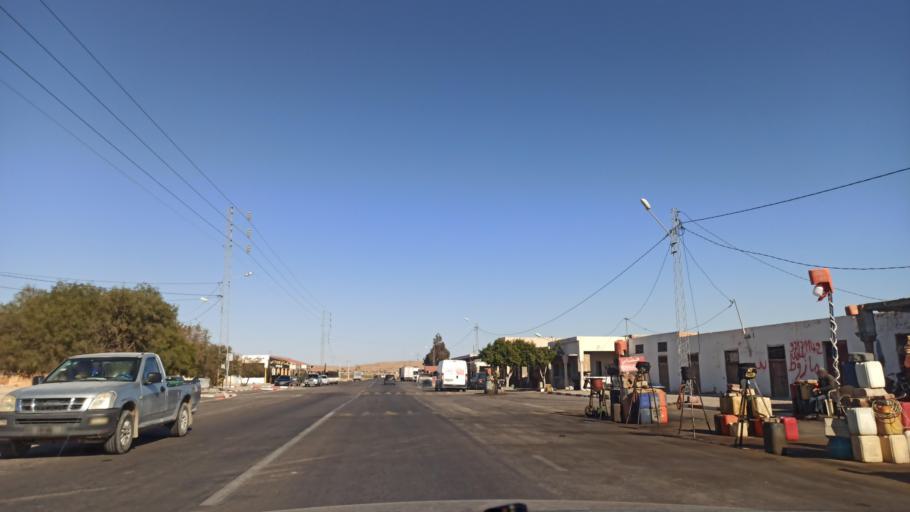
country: TN
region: Sidi Bu Zayd
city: Bi'r al Hufayy
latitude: 34.7042
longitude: 9.0449
